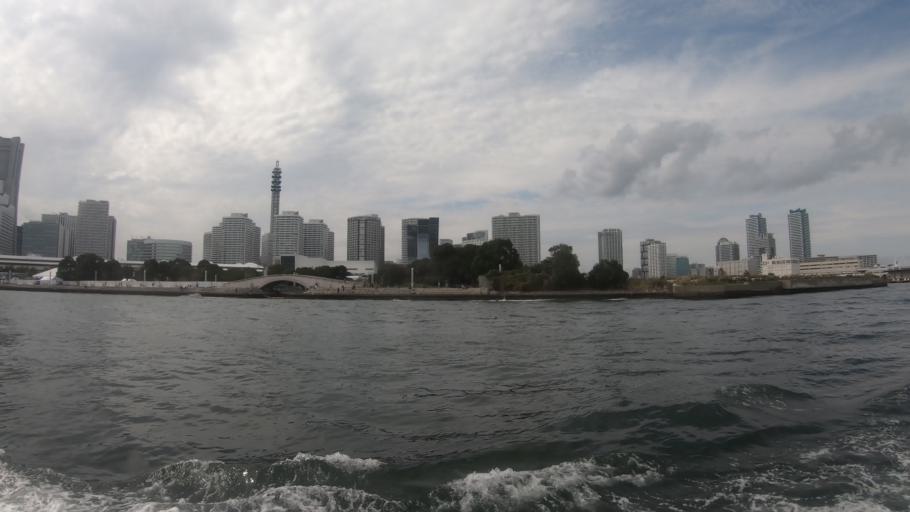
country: JP
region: Kanagawa
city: Yokohama
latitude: 35.4625
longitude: 139.6396
